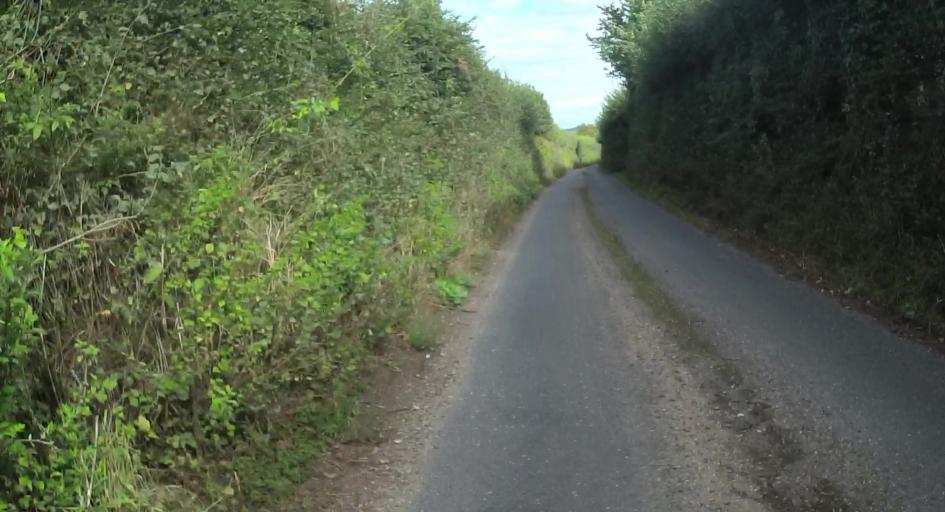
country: GB
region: England
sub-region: West Berkshire
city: Thatcham
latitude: 51.3738
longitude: -1.2136
